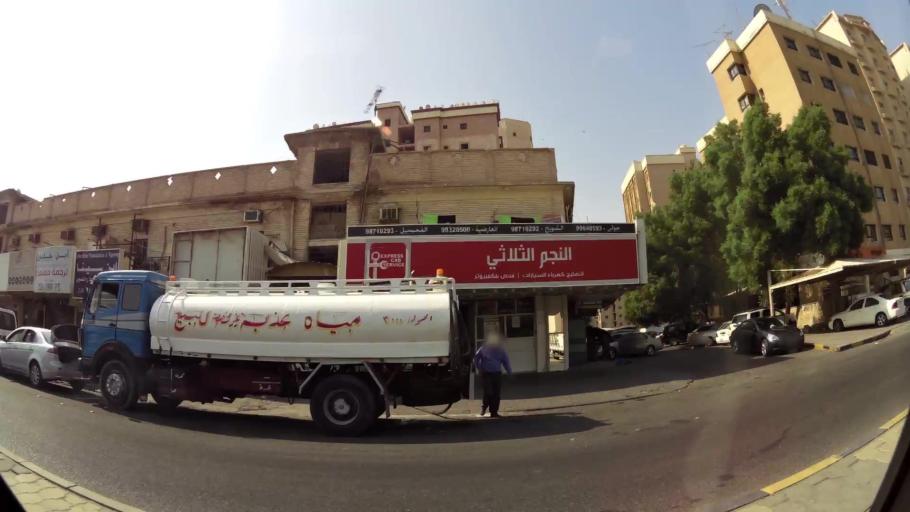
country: KW
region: Muhafazat Hawalli
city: Hawalli
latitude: 29.3442
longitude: 48.0206
